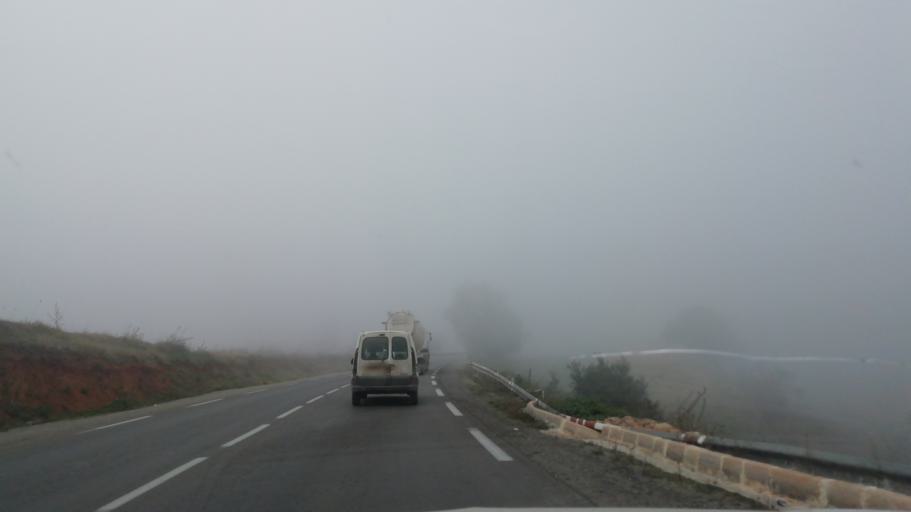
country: DZ
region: Mascara
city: Mascara
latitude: 35.5207
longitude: 0.3187
